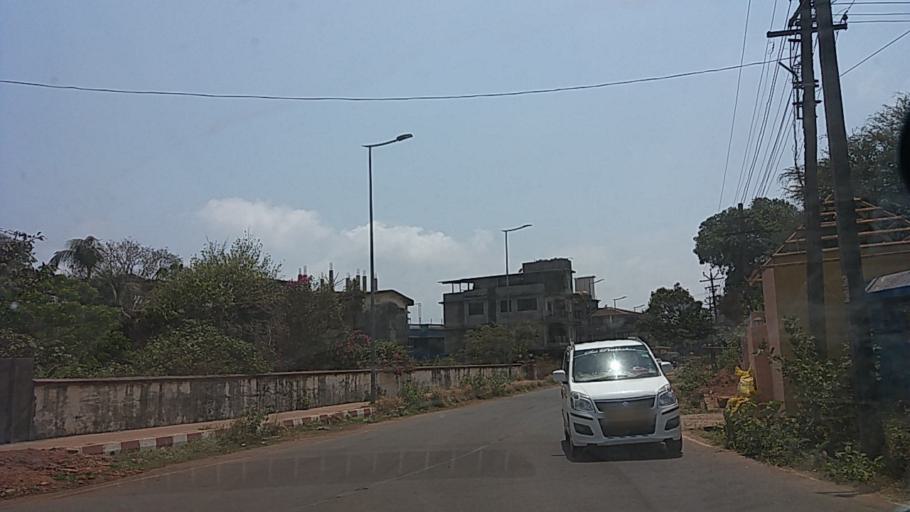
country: IN
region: Goa
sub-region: North Goa
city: Serula
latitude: 15.5284
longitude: 73.8339
